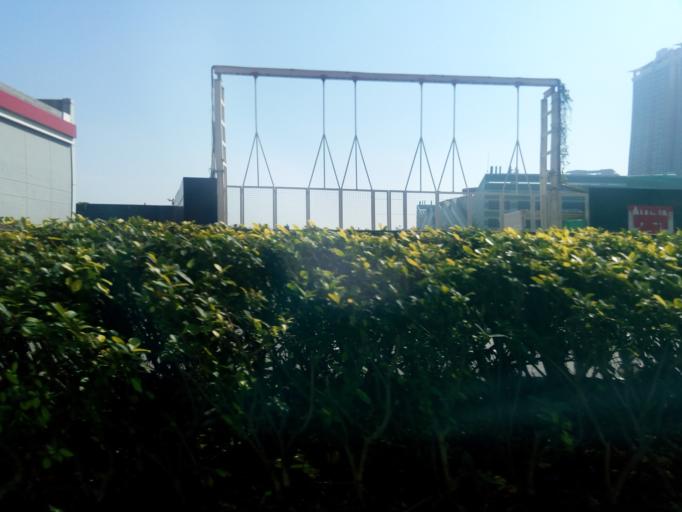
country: MO
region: Macau
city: Macau
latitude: 22.2098
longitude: 113.5575
